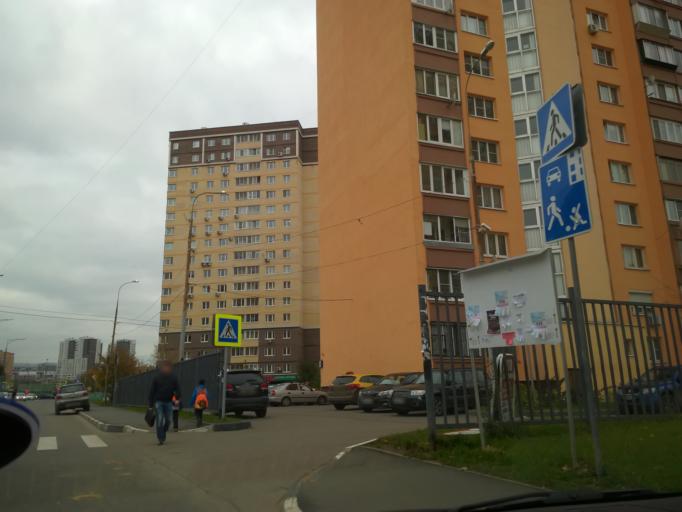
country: RU
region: Moskovskaya
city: Kommunarka
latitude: 55.5696
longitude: 37.4737
